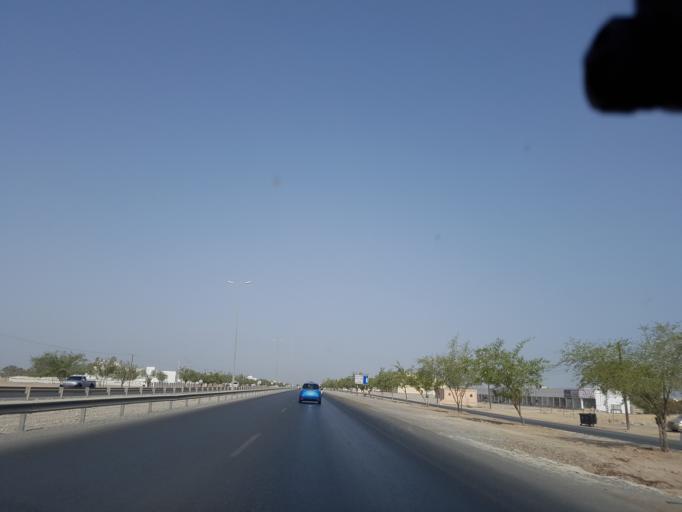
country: OM
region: Al Batinah
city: As Suwayq
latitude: 23.7411
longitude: 57.6387
